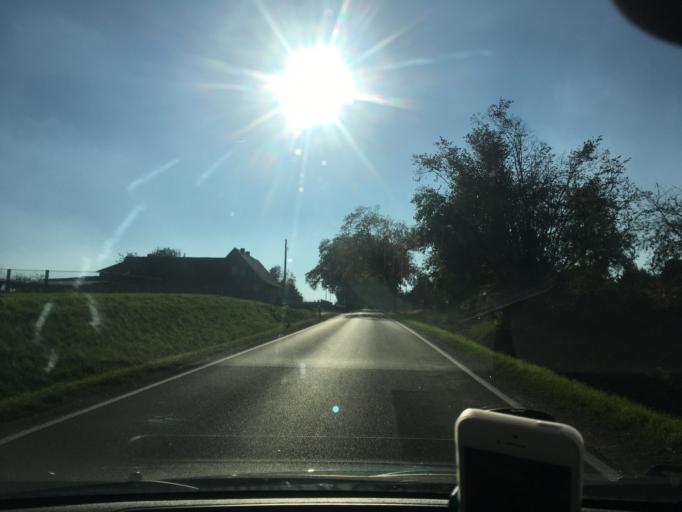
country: DE
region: Mecklenburg-Vorpommern
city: Stralendorf
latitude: 53.5685
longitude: 11.2783
